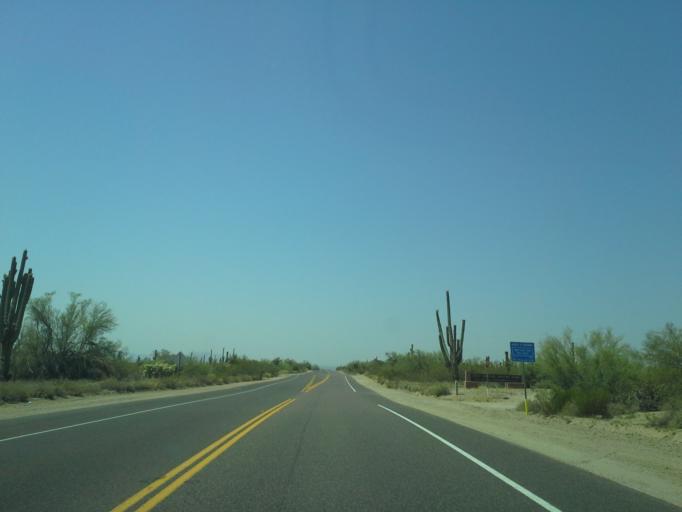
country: US
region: Arizona
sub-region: Pinal County
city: Apache Junction
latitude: 33.4882
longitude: -111.6202
